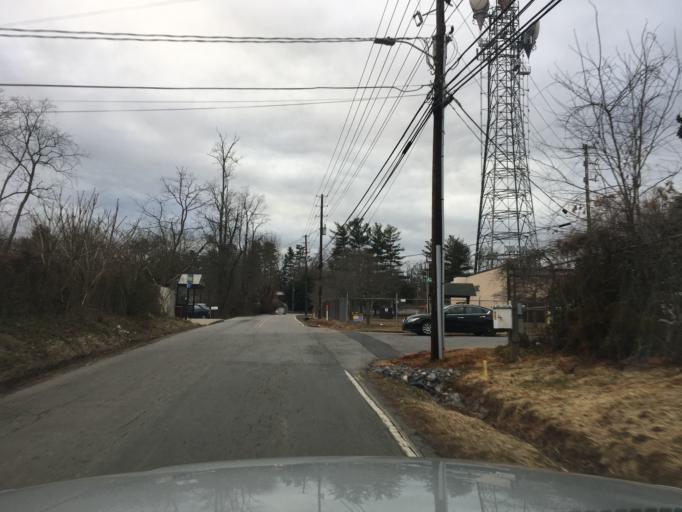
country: US
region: North Carolina
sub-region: Buncombe County
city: Asheville
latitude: 35.6006
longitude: -82.5843
